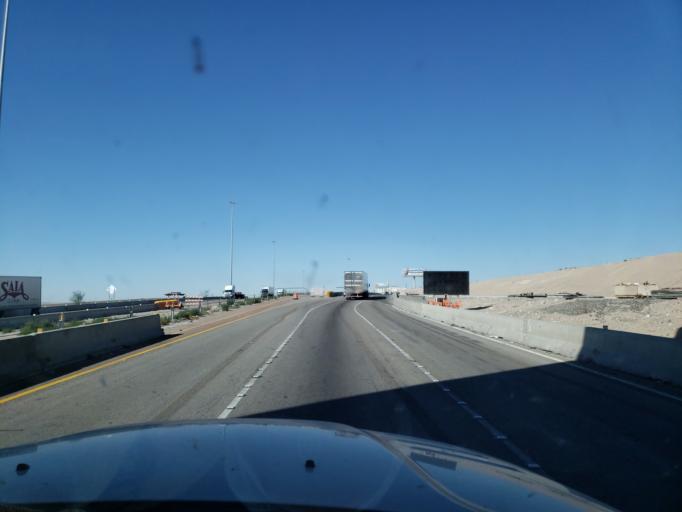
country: US
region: New Mexico
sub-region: Dona Ana County
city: Sunland Park
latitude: 31.8256
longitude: -106.5597
